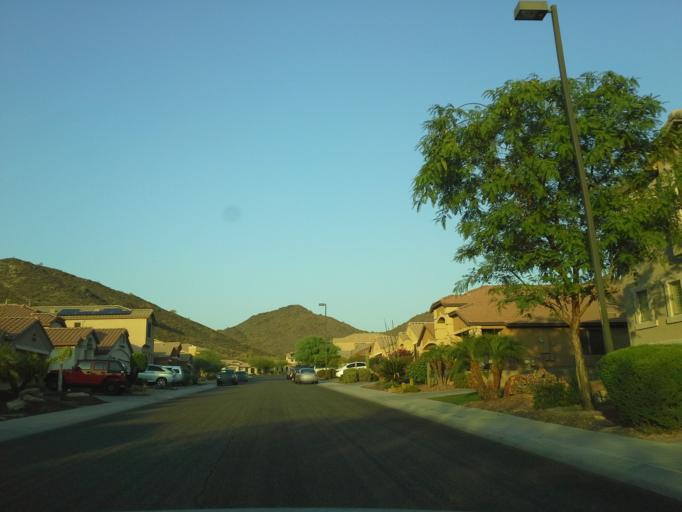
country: US
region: Arizona
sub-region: Maricopa County
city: Anthem
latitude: 33.7520
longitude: -112.1031
